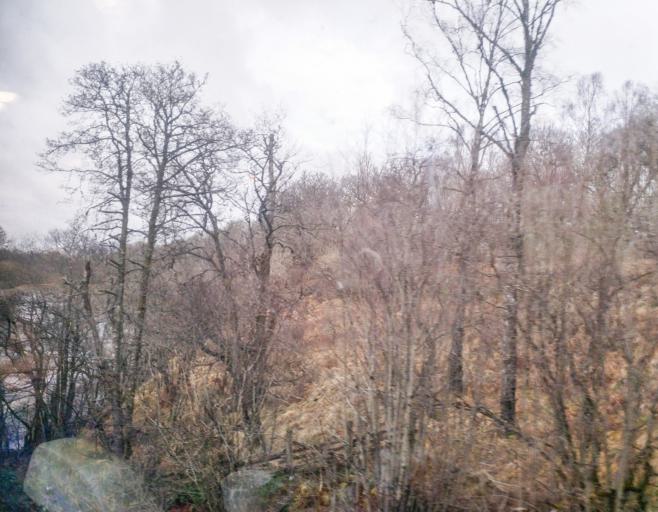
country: GB
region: Scotland
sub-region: Highland
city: Spean Bridge
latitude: 56.8934
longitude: -4.8925
